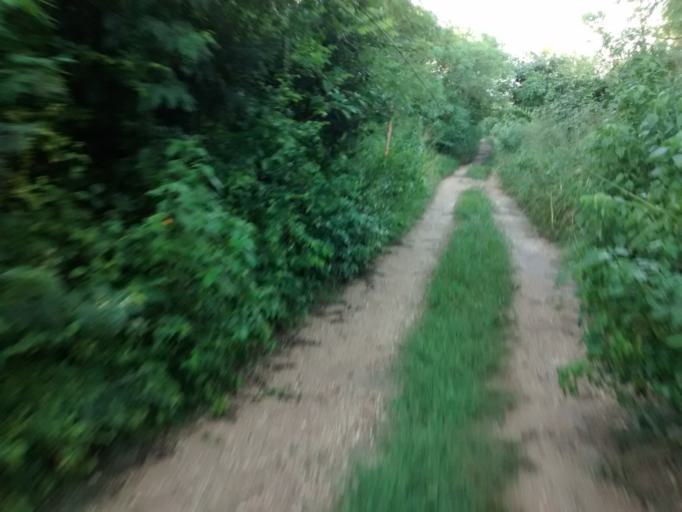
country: MX
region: Yucatan
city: Valladolid
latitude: 20.7163
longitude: -88.2062
